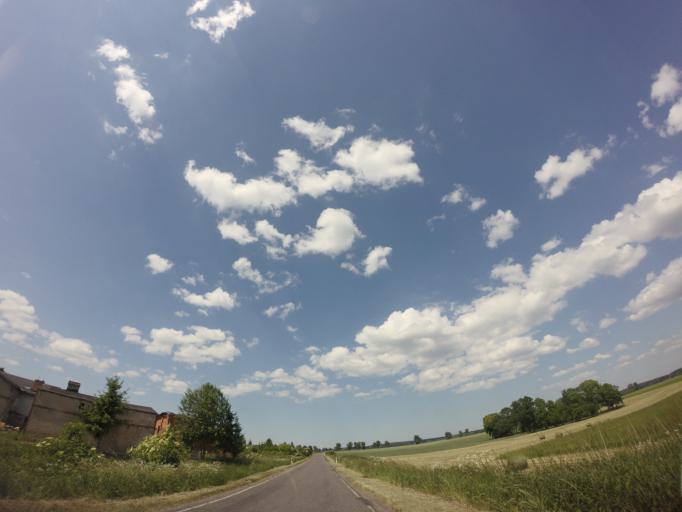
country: PL
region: West Pomeranian Voivodeship
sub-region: Powiat stargardzki
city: Dolice
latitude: 53.1450
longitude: 15.2427
